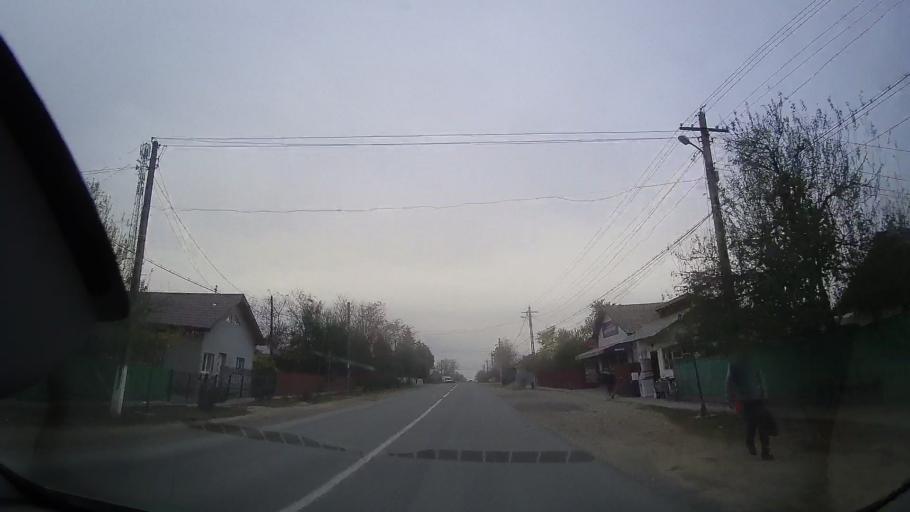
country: RO
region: Ialomita
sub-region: Comuna Grivita
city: Grivita
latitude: 44.7371
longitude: 27.2872
